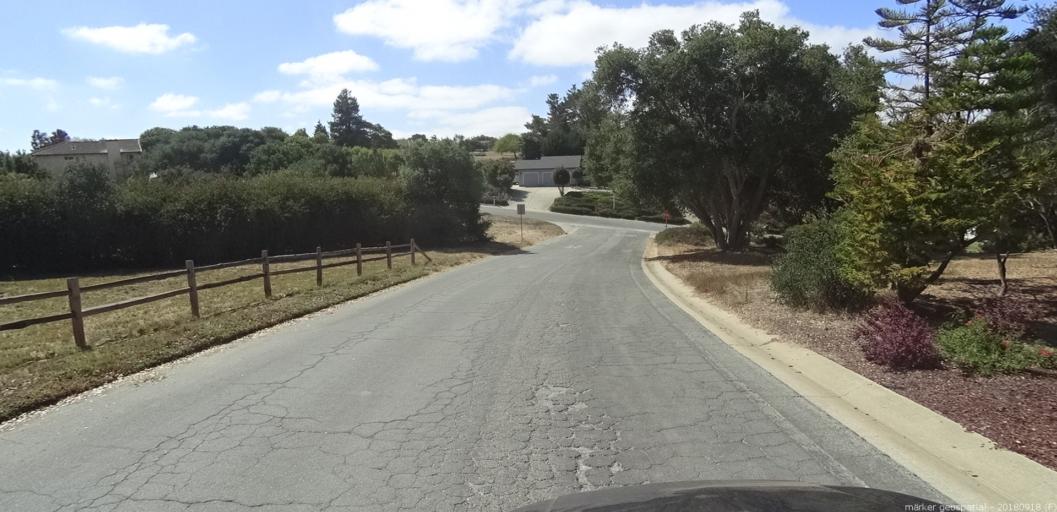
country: US
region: California
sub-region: Monterey County
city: Prunedale
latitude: 36.7640
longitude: -121.6606
